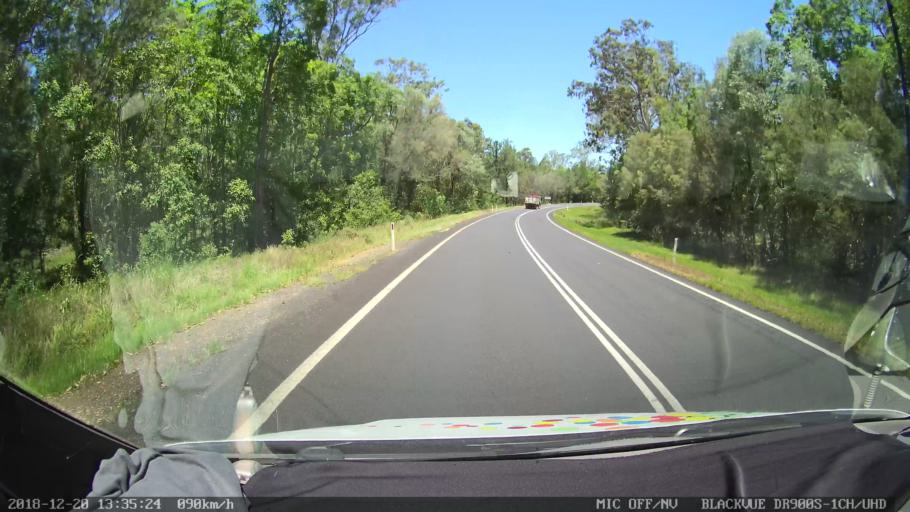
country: AU
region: New South Wales
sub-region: Clarence Valley
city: Gordon
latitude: -29.2689
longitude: 152.9912
